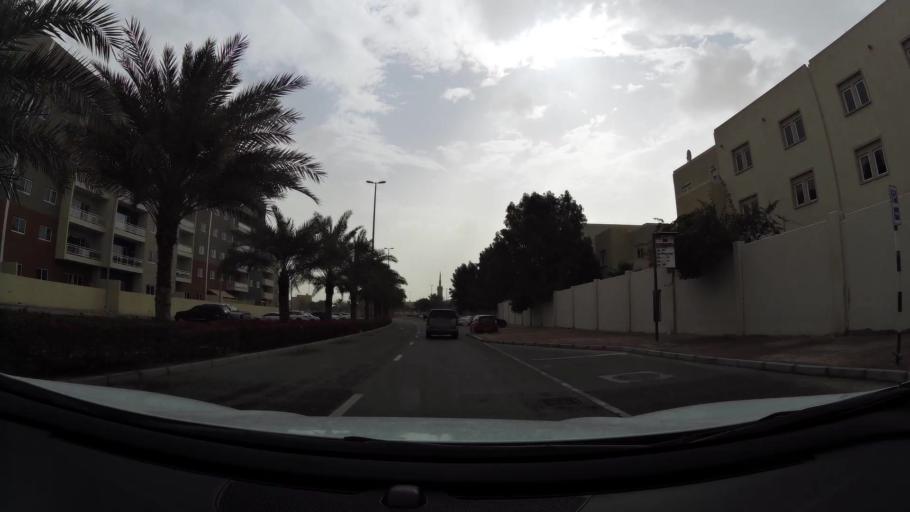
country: AE
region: Abu Dhabi
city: Abu Dhabi
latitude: 24.4543
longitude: 54.6726
